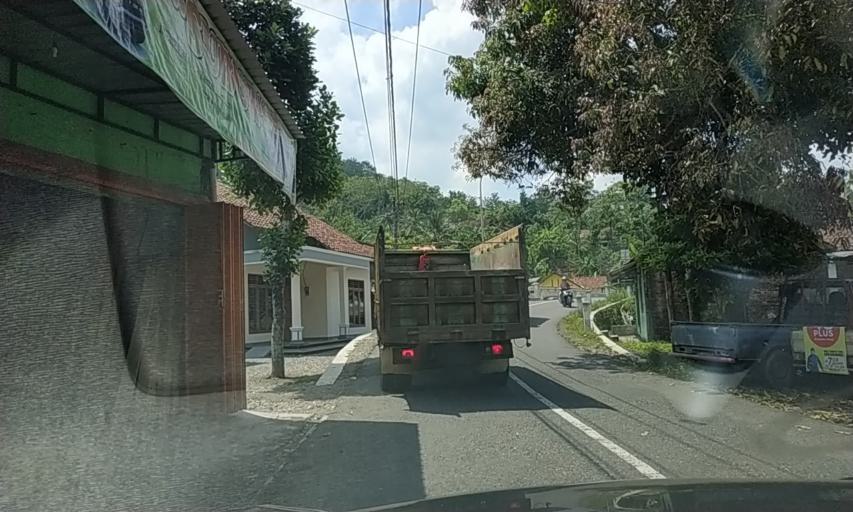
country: ID
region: Central Java
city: Gombong
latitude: -7.6330
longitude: 109.7086
